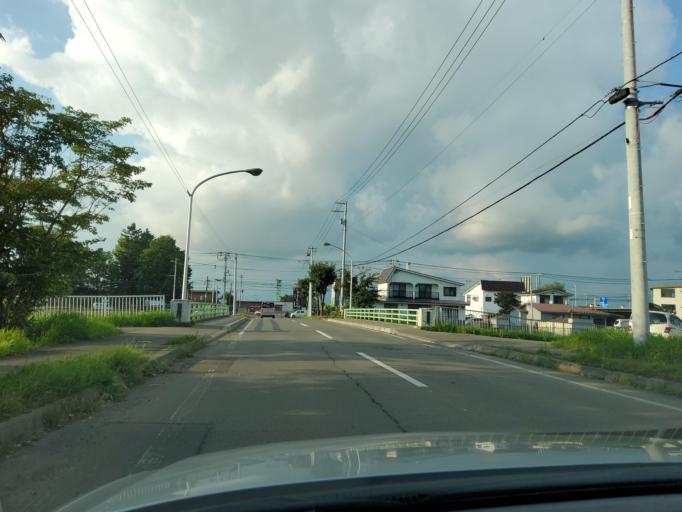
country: JP
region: Hokkaido
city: Obihiro
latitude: 42.9196
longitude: 143.1848
